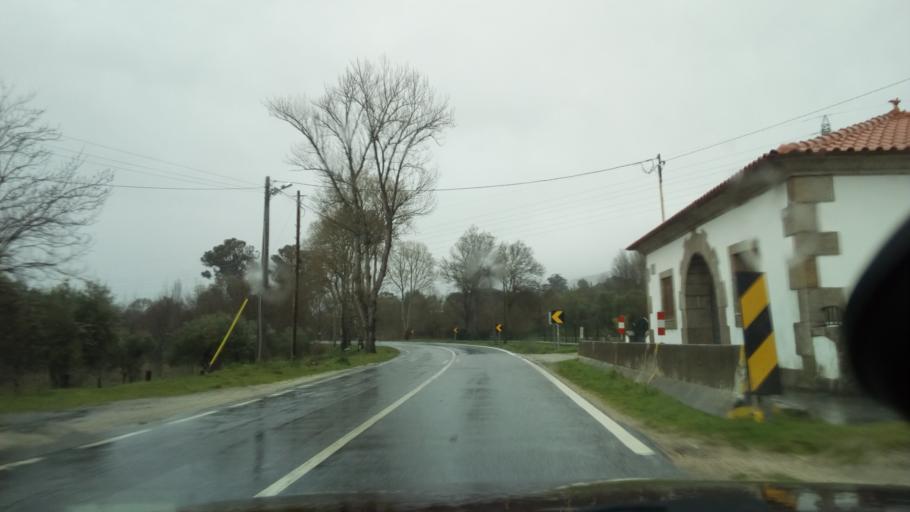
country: PT
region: Guarda
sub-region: Fornos de Algodres
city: Fornos de Algodres
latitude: 40.5350
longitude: -7.5528
